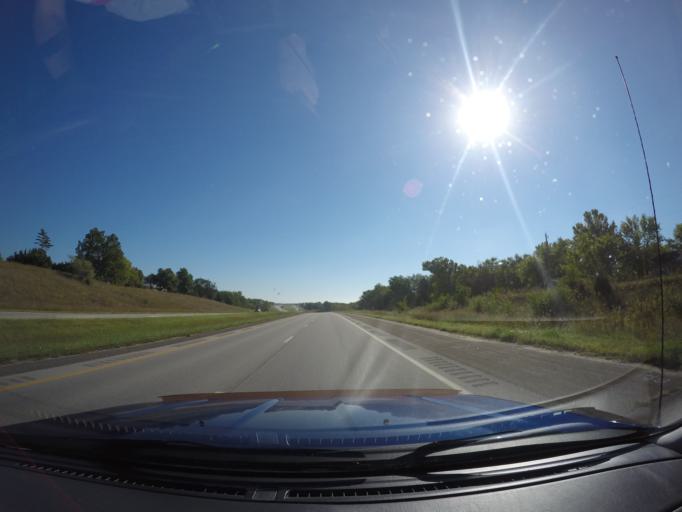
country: US
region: Kansas
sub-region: Riley County
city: Manhattan
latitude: 39.1986
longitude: -96.4532
